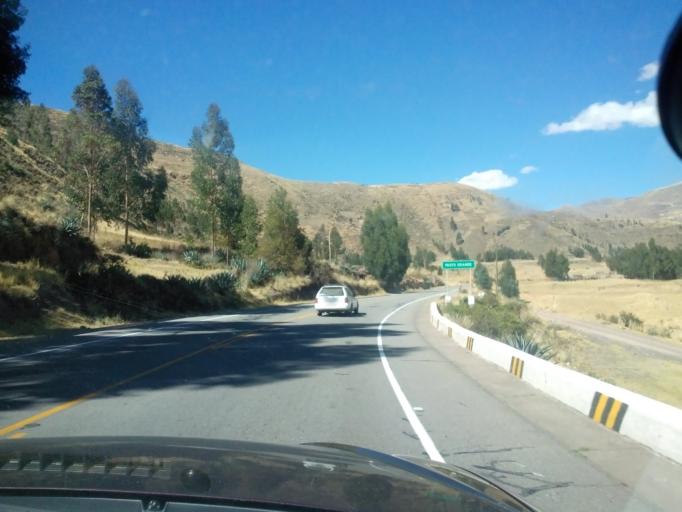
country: PE
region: Cusco
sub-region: Provincia de Canchis
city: Combapata
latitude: -14.0785
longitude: -71.4380
